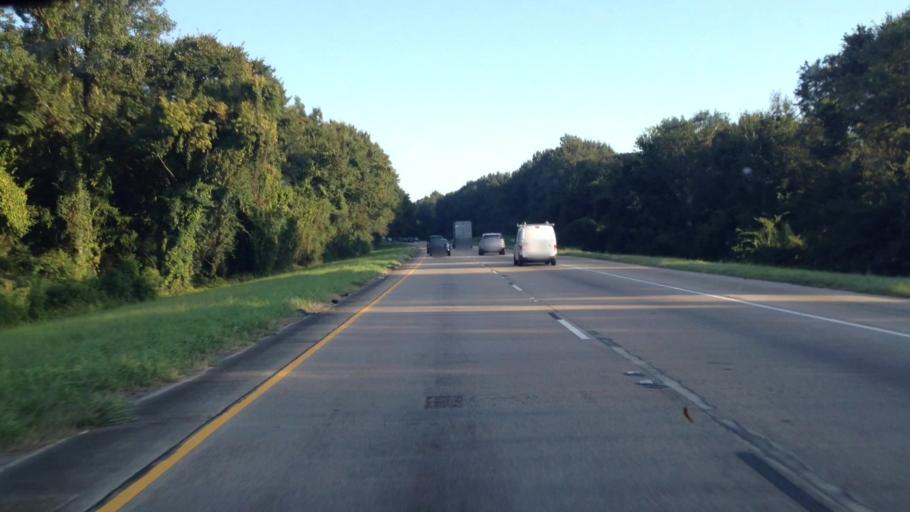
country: US
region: Louisiana
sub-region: Ascension Parish
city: Prairieville
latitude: 30.3056
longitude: -90.9934
